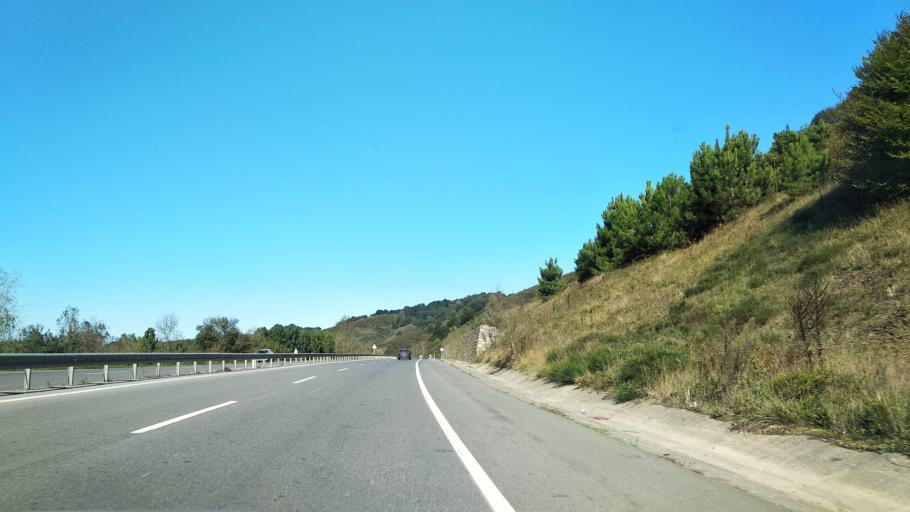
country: TR
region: Sakarya
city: Karasu
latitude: 41.0619
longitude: 30.6384
